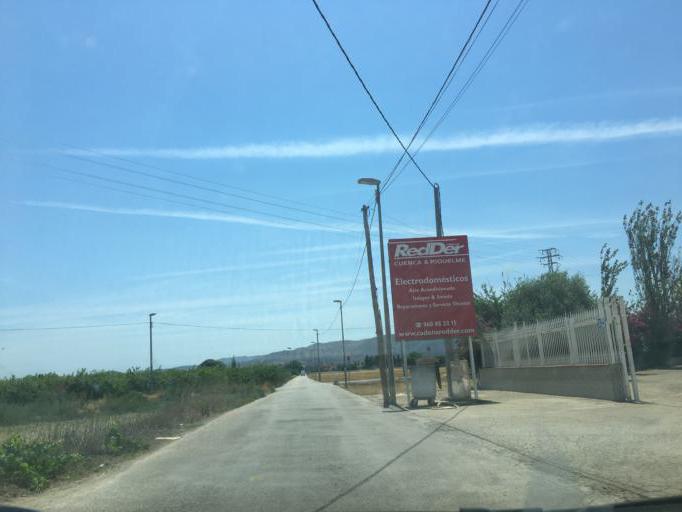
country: ES
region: Murcia
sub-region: Murcia
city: Santomera
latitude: 38.0288
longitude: -1.0627
